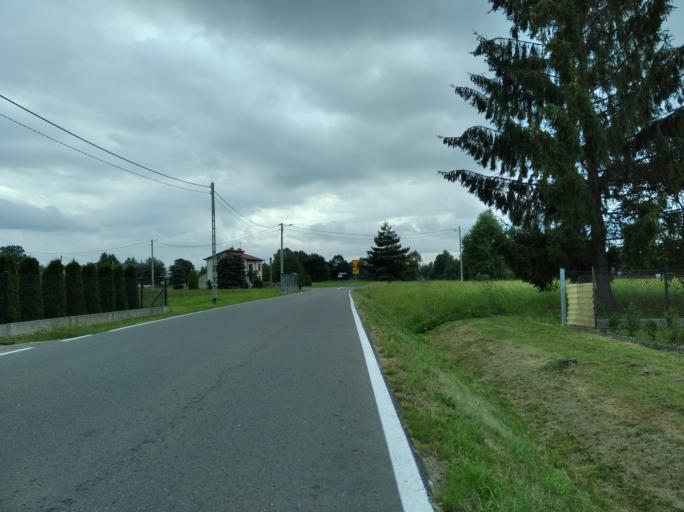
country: PL
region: Subcarpathian Voivodeship
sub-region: Powiat krosnienski
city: Odrzykon
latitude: 49.7410
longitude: 21.7313
